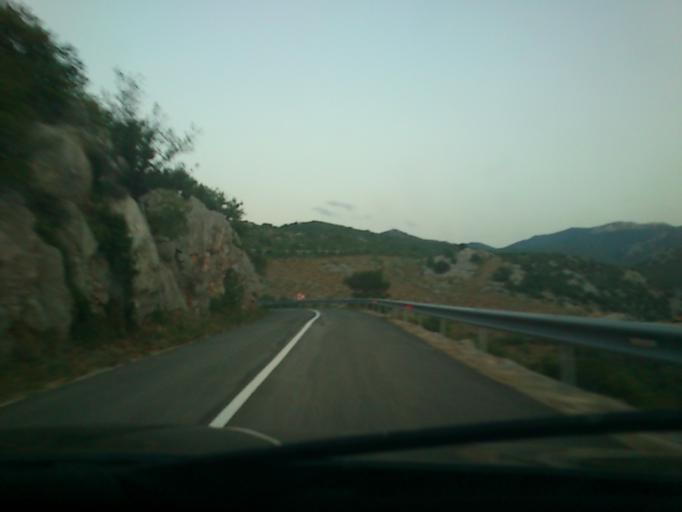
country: HR
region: Licko-Senjska
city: Senj
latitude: 44.9184
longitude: 14.9223
